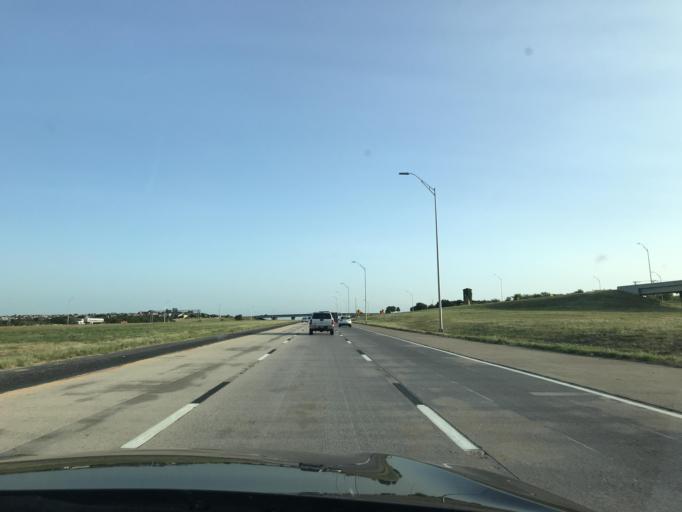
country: US
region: Texas
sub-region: Tarrant County
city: Benbrook
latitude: 32.6968
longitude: -97.4703
